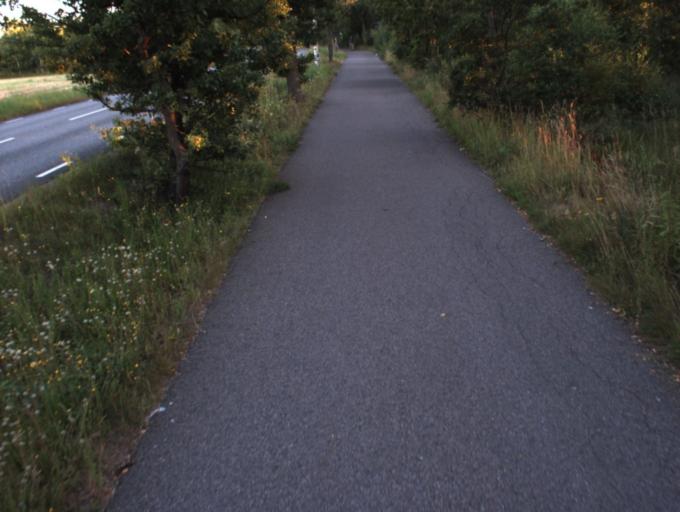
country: SE
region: Skane
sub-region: Helsingborg
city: Helsingborg
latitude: 56.0746
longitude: 12.6922
